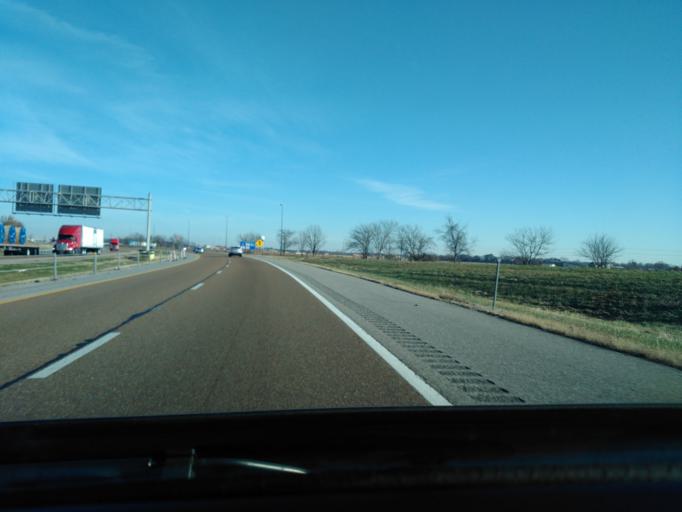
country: US
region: Illinois
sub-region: Madison County
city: Troy
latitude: 38.7195
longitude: -89.9167
